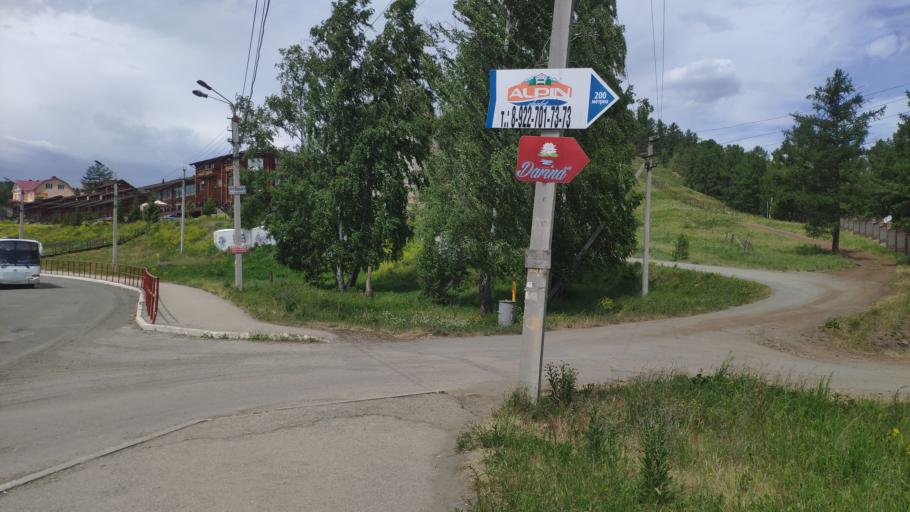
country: RU
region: Bashkortostan
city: Abzakovo
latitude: 53.8119
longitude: 58.6349
